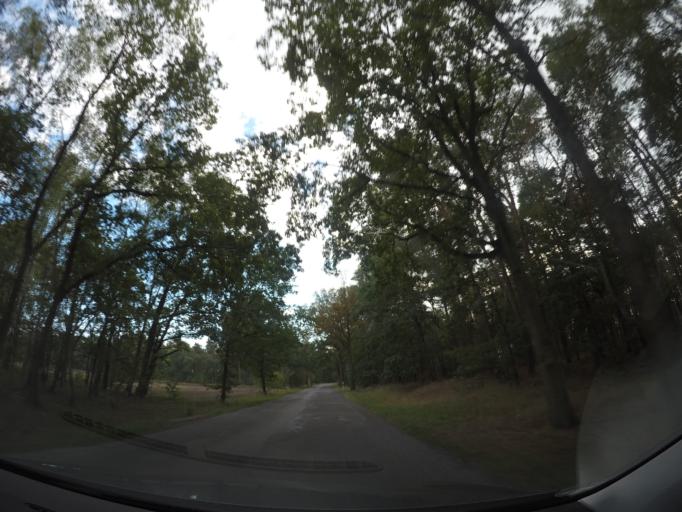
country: DE
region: Saxony-Anhalt
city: Mieste
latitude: 52.4748
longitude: 11.1357
